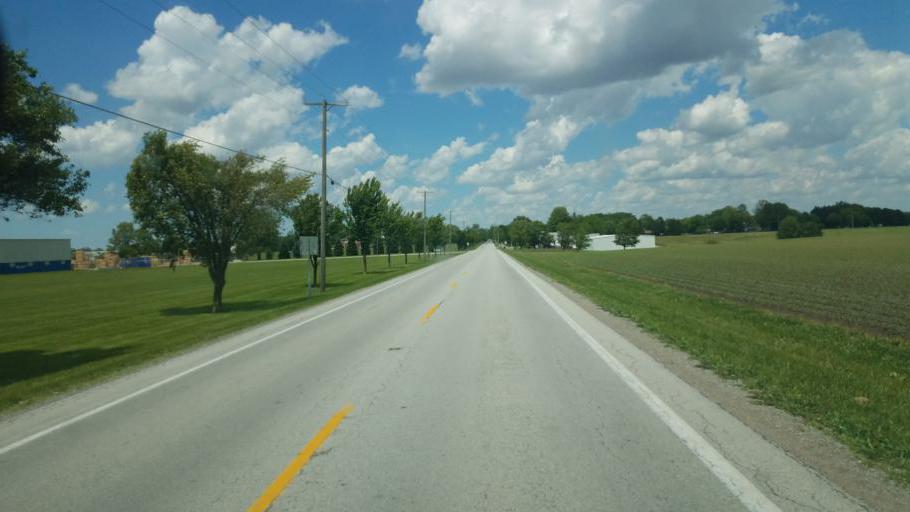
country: US
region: Ohio
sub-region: Wyandot County
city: Upper Sandusky
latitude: 40.8086
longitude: -83.2841
